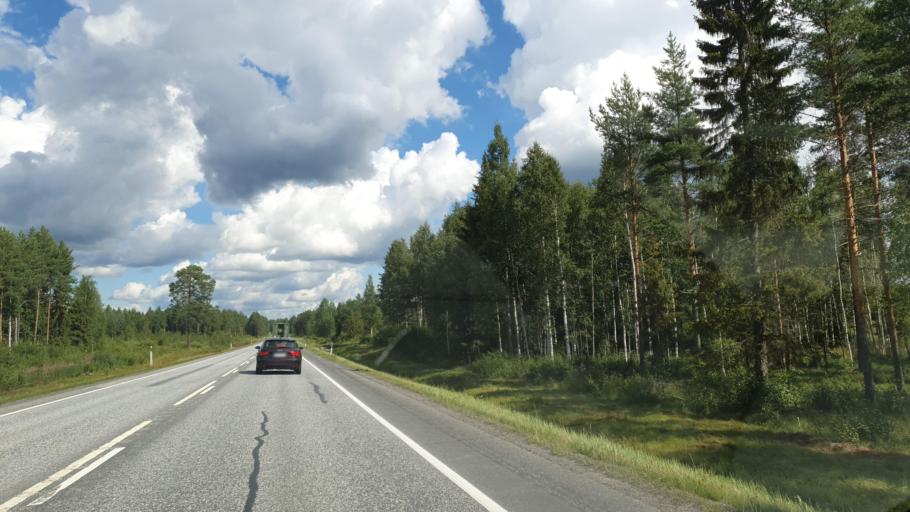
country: FI
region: Kainuu
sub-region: Kajaani
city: Kajaani
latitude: 64.1307
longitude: 27.4798
